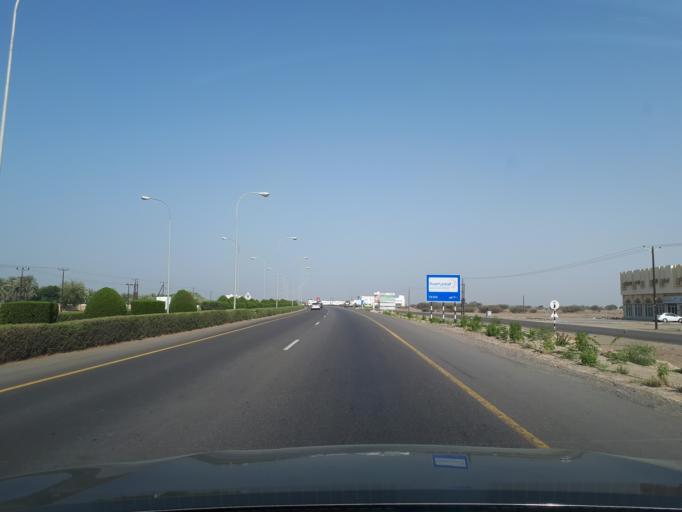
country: OM
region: Al Batinah
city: Al Sohar
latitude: 24.4131
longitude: 56.6334
